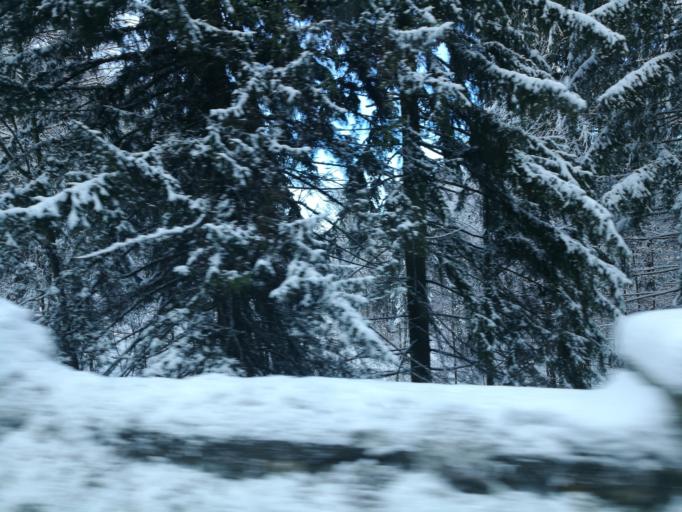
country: RO
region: Brasov
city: Brasov
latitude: 45.6029
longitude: 25.5545
